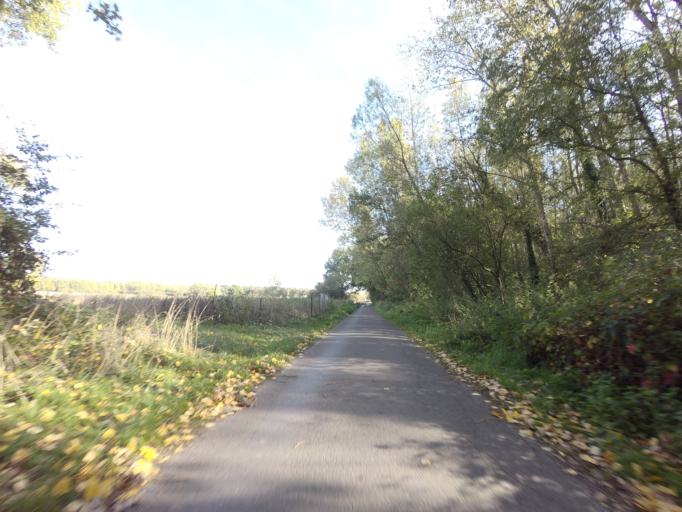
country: BE
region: Flanders
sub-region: Provincie Vlaams-Brabant
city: Kampenhout
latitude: 50.9229
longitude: 4.5937
